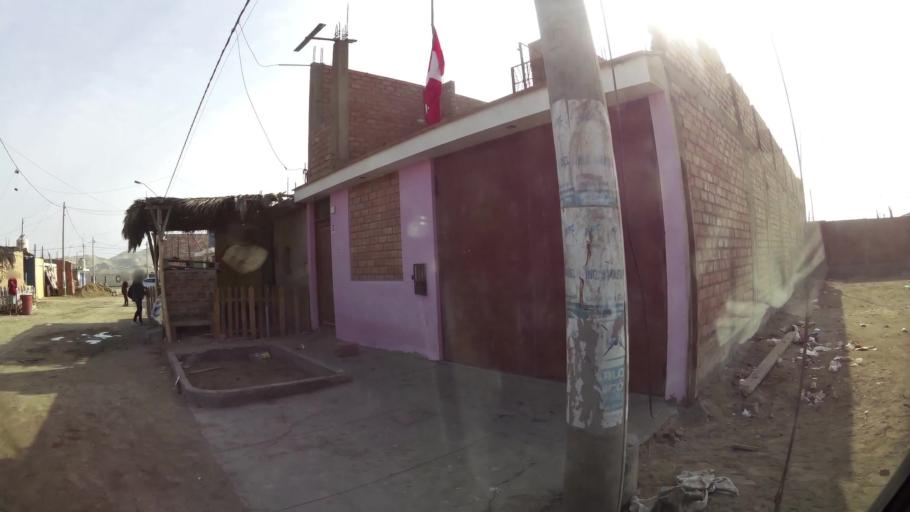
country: PE
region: Lima
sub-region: Lima
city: Santa Rosa
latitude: -11.7661
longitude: -77.1652
